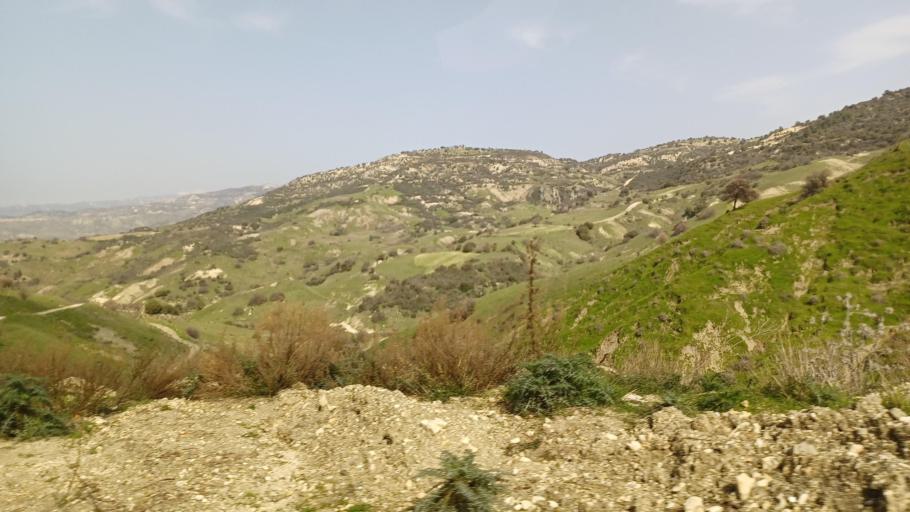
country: CY
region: Limassol
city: Pissouri
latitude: 34.7486
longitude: 32.6610
